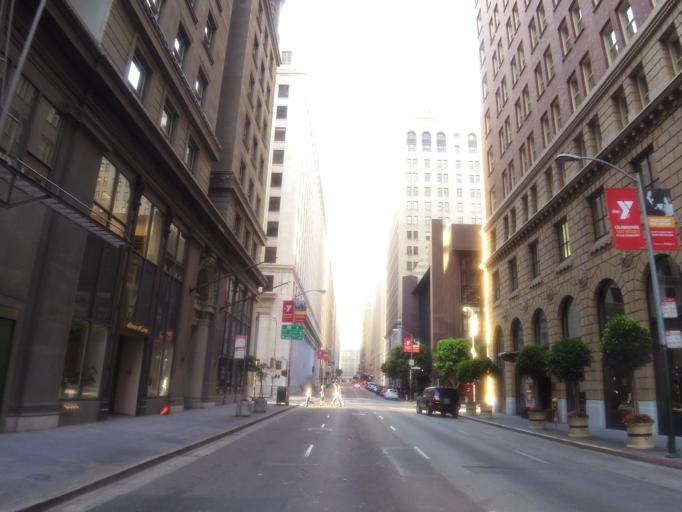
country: US
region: California
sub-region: San Francisco County
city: San Francisco
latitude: 37.7934
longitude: -122.4029
